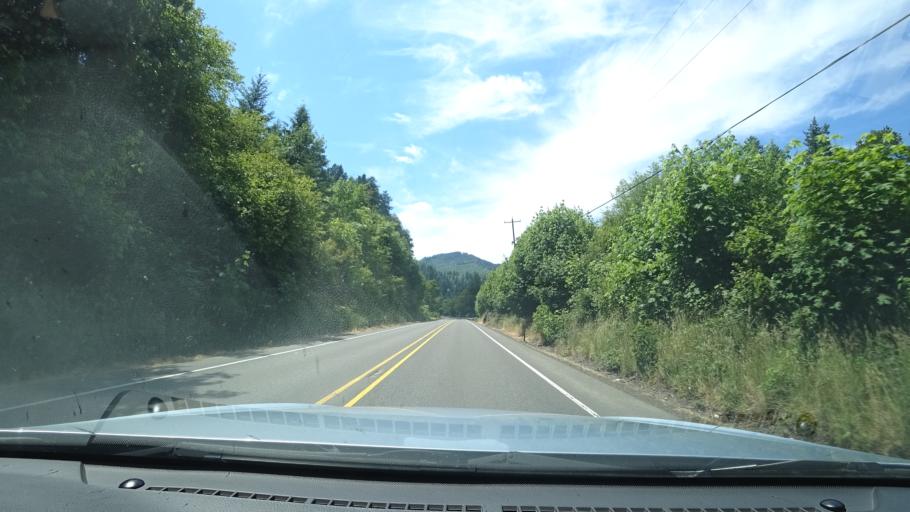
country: US
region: Oregon
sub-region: Lane County
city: Florence
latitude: 44.0324
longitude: -123.8505
